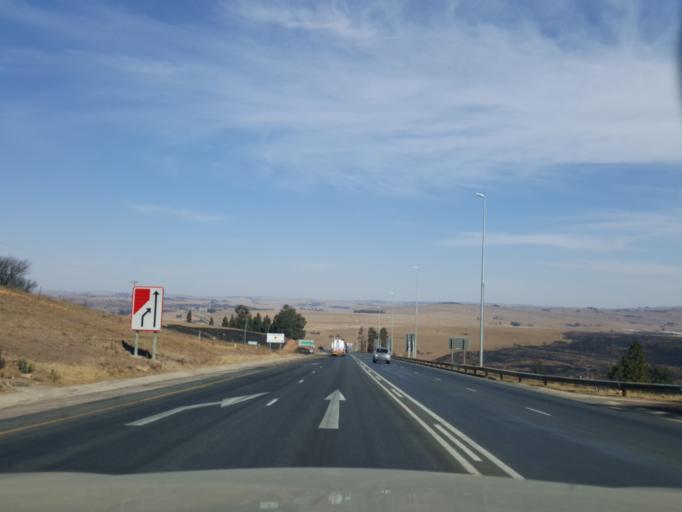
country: ZA
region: Mpumalanga
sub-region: Nkangala District Municipality
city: Belfast
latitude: -25.6296
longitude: 30.2571
